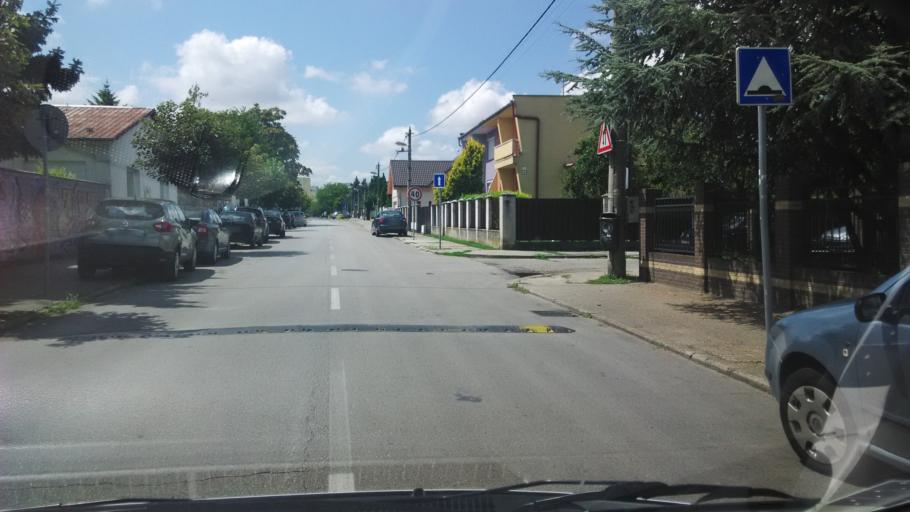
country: SK
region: Trnavsky
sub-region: Okres Trnava
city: Trnava
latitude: 48.3716
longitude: 17.5811
